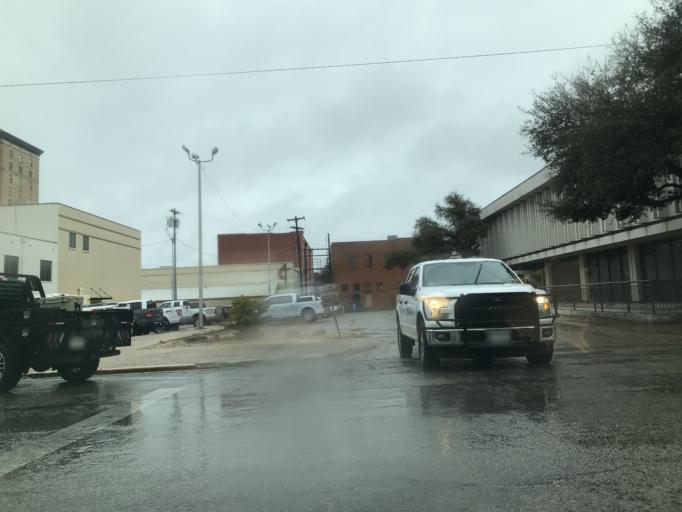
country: US
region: Texas
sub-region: Tom Green County
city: San Angelo
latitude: 31.4627
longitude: -100.4362
